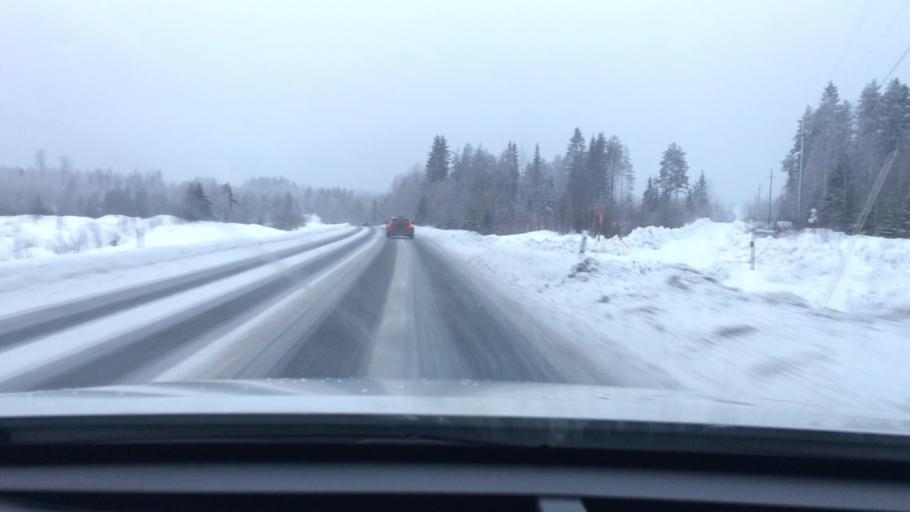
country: FI
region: Northern Savo
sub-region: Ylae-Savo
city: Sonkajaervi
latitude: 63.7591
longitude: 27.3984
